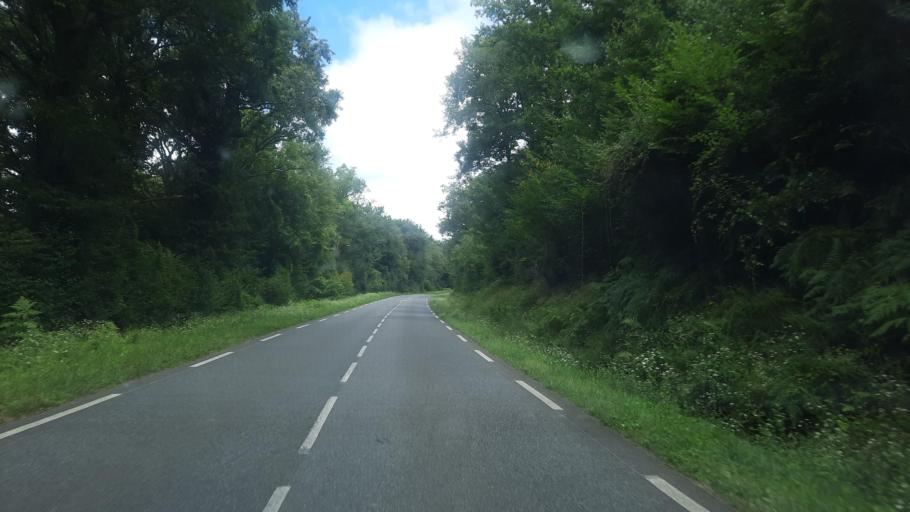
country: FR
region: Midi-Pyrenees
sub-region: Departement des Hautes-Pyrenees
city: Trie-sur-Baise
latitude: 43.2995
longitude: 0.4345
